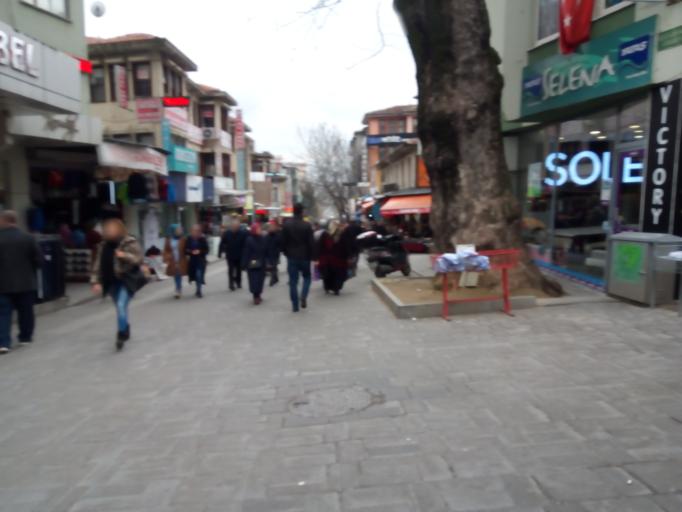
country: TR
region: Bursa
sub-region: Osmangazi
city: Bursa
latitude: 40.1861
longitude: 29.0610
